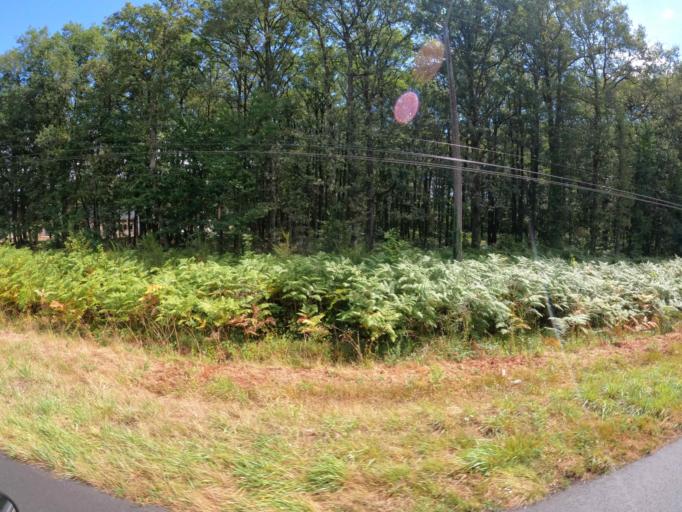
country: FR
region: Pays de la Loire
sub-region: Departement de Maine-et-Loire
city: Feneu
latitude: 47.5837
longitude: -0.5911
